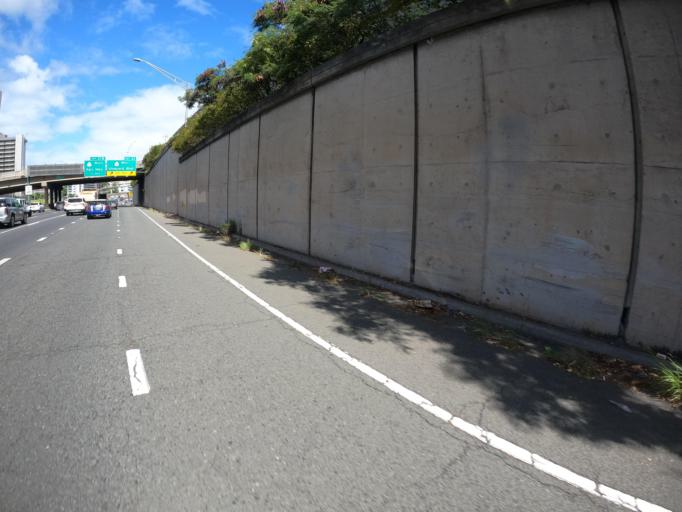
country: US
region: Hawaii
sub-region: Honolulu County
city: Honolulu
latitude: 21.3057
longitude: -157.8480
